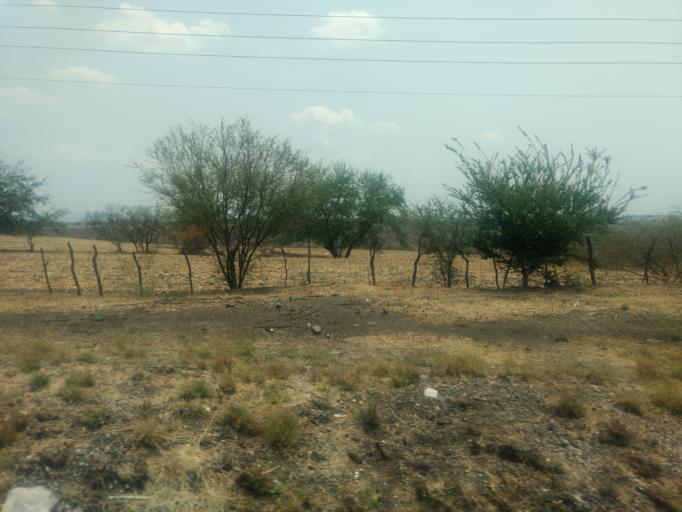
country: MX
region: Morelos
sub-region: Amacuzac
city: Amacuzac
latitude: 18.6281
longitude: -99.3749
